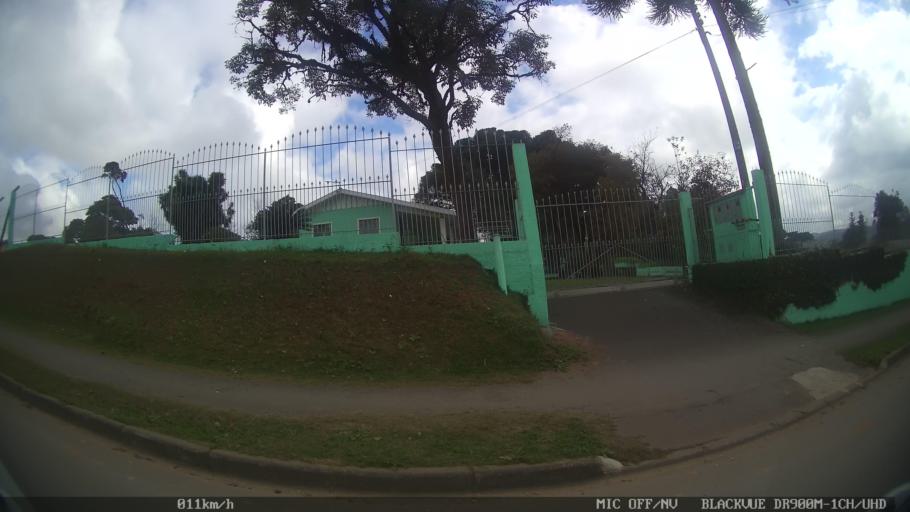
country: BR
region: Parana
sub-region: Colombo
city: Colombo
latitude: -25.3439
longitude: -49.2428
